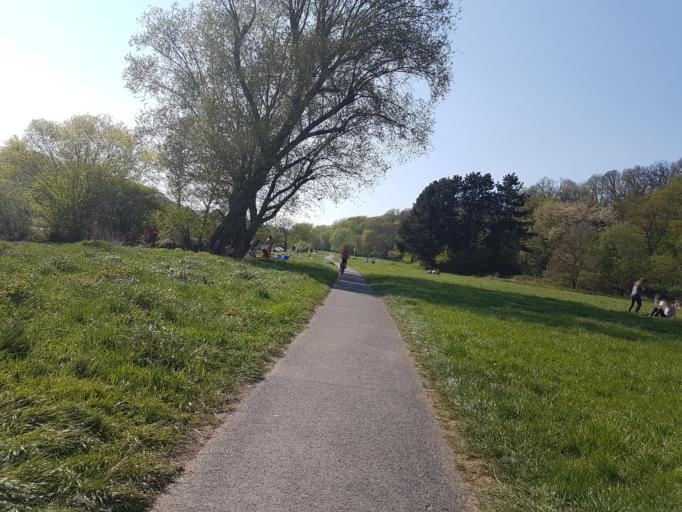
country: DE
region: North Rhine-Westphalia
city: Hattingen
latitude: 51.4124
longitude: 7.2431
